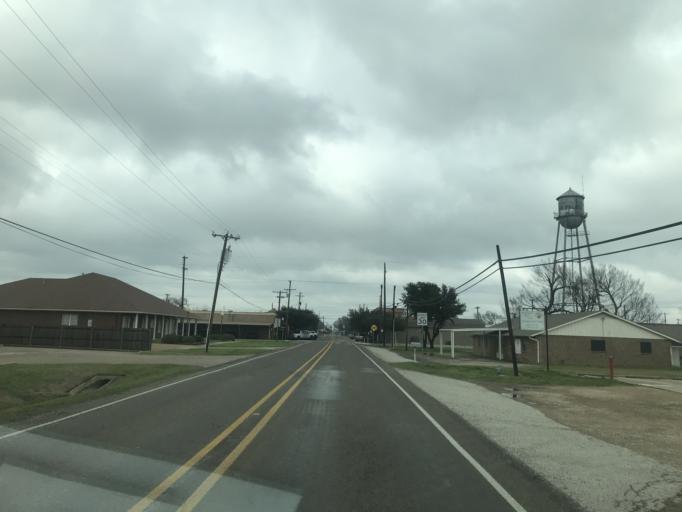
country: US
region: Texas
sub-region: Ellis County
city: Palmer
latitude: 32.4307
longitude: -96.6702
